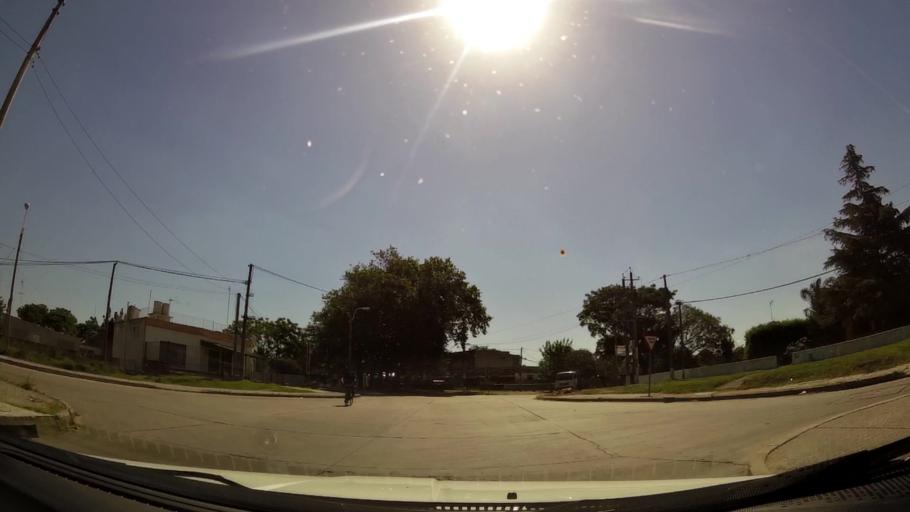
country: UY
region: Canelones
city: La Paz
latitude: -34.8359
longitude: -56.2553
